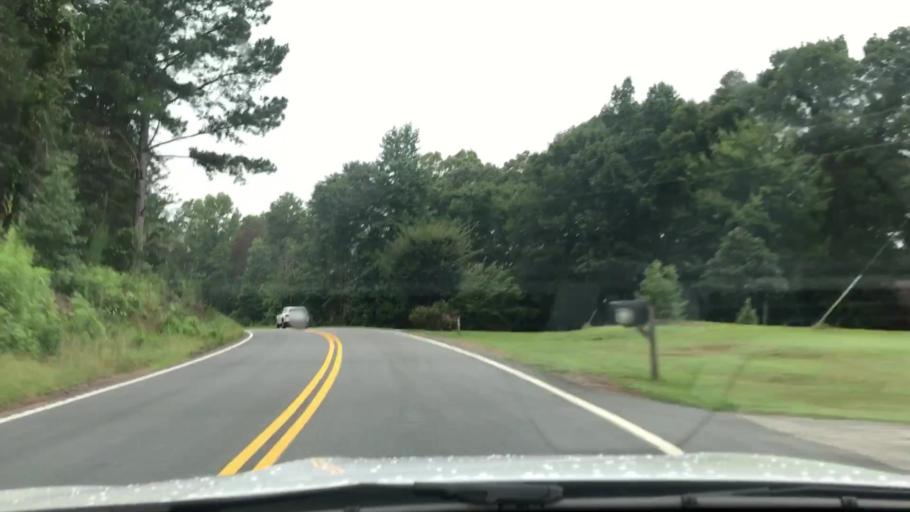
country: US
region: South Carolina
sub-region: Spartanburg County
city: Roebuck
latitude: 34.8261
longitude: -81.9476
